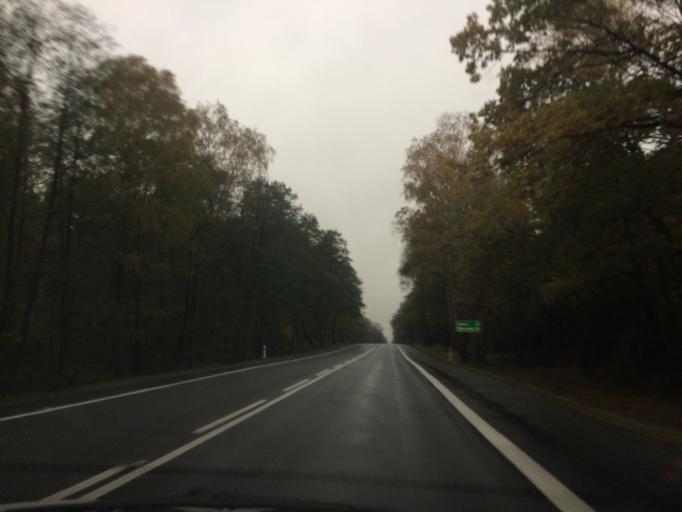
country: PL
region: Masovian Voivodeship
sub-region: Powiat otwocki
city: Kolbiel
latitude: 52.0805
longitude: 21.4395
